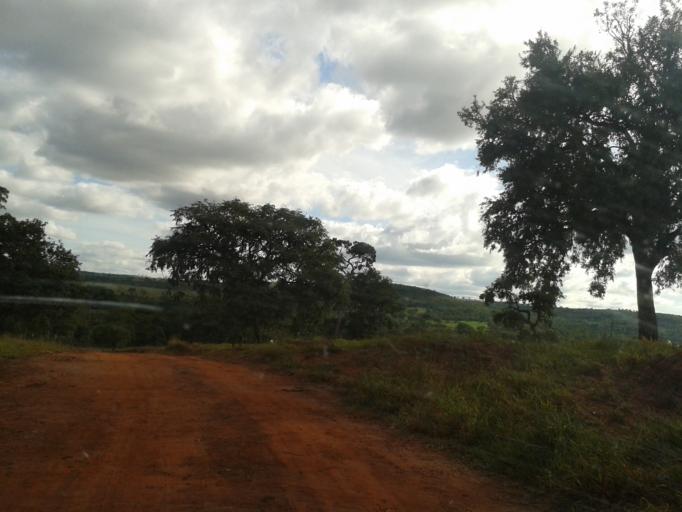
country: BR
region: Minas Gerais
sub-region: Campina Verde
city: Campina Verde
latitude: -19.4388
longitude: -49.7290
